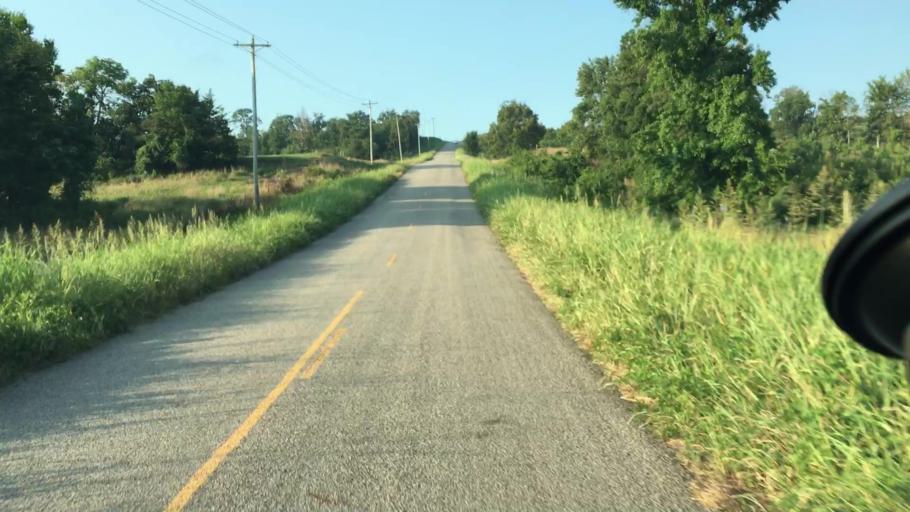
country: US
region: Arkansas
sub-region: Johnson County
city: Coal Hill
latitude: 35.3616
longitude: -93.6131
